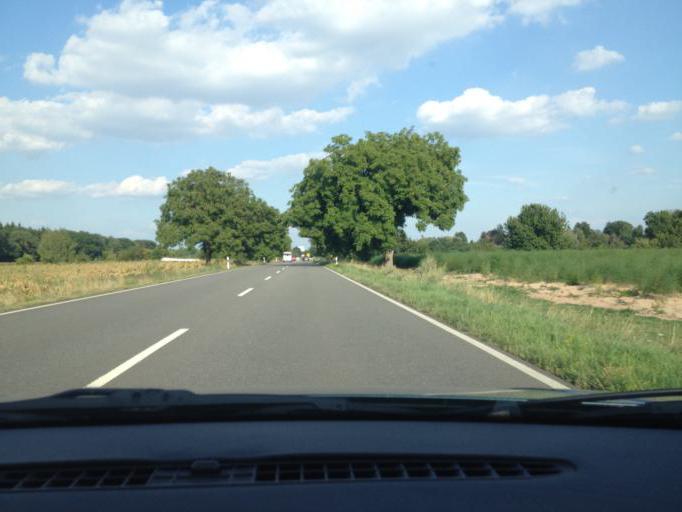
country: DE
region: Rheinland-Pfalz
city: Dudenhofen
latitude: 49.3182
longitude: 8.3746
